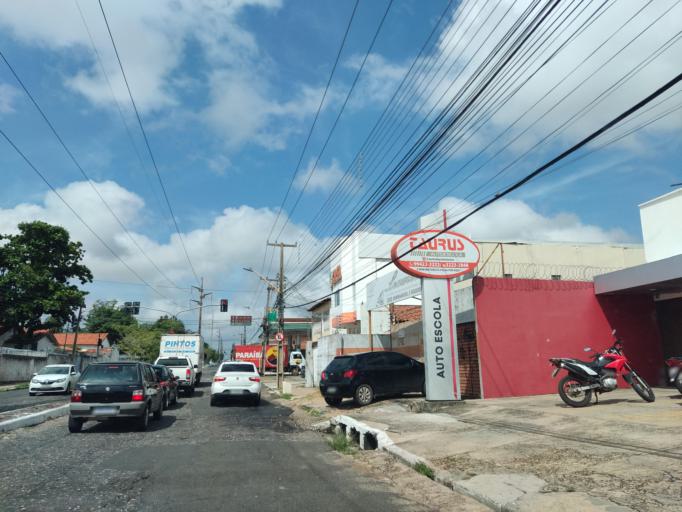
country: BR
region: Piaui
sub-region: Teresina
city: Teresina
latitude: -5.0733
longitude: -42.8101
